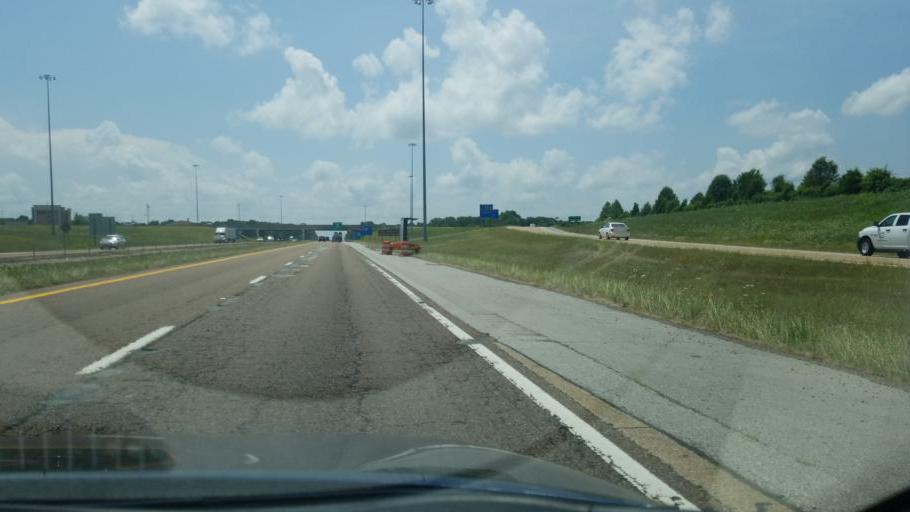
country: US
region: Tennessee
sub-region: Madison County
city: Jackson
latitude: 35.6752
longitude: -88.8042
